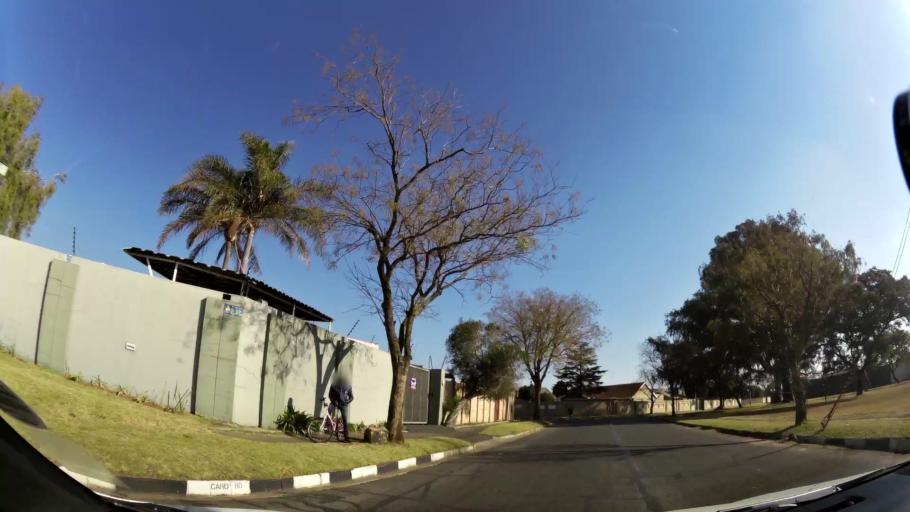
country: ZA
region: Gauteng
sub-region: City of Johannesburg Metropolitan Municipality
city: Johannesburg
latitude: -26.2516
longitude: 28.0094
